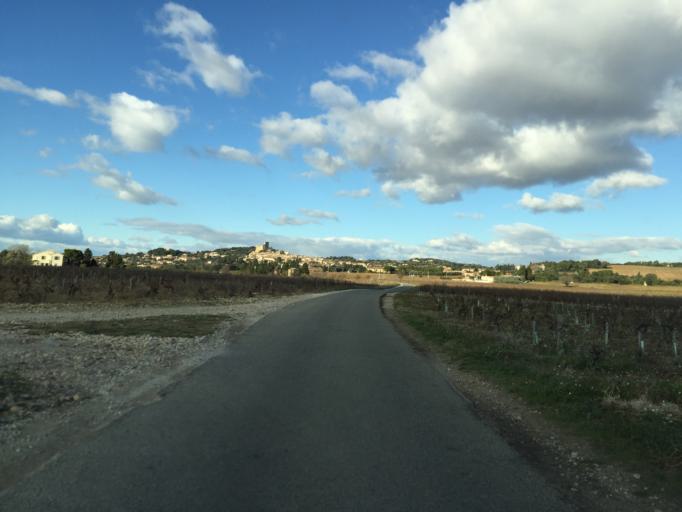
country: FR
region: Provence-Alpes-Cote d'Azur
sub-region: Departement du Vaucluse
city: Chateauneuf-du-Pape
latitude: 44.0405
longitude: 4.8364
